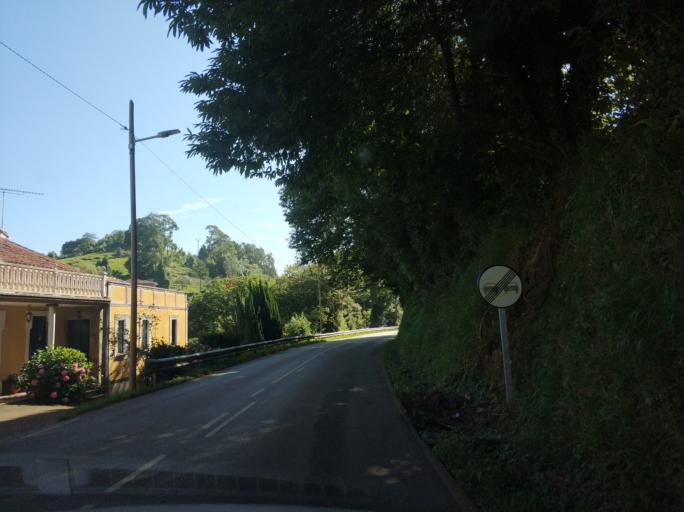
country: ES
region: Asturias
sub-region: Province of Asturias
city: Cudillero
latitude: 43.5464
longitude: -6.2208
